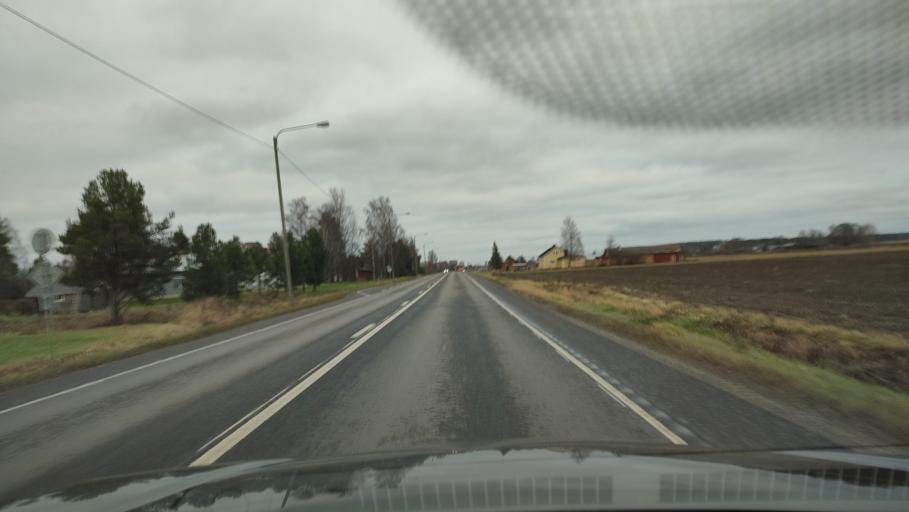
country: FI
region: Southern Ostrobothnia
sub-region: Seinaejoki
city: Ilmajoki
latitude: 62.7020
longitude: 22.5175
